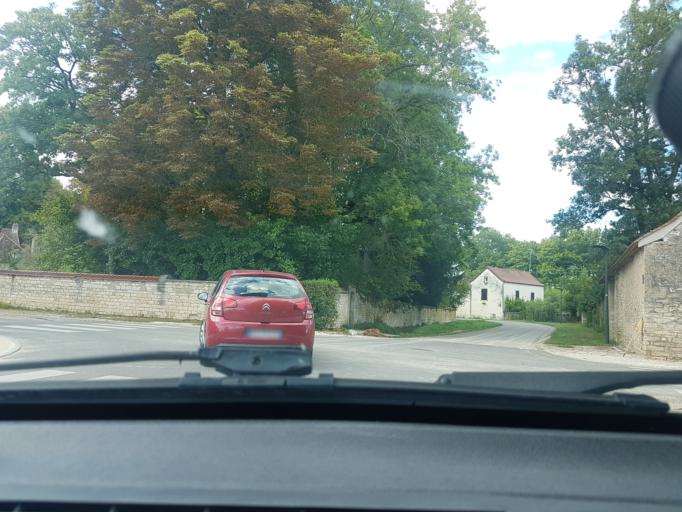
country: FR
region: Bourgogne
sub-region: Departement de Saone-et-Loire
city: Fontaines
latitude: 46.8495
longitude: 4.7605
